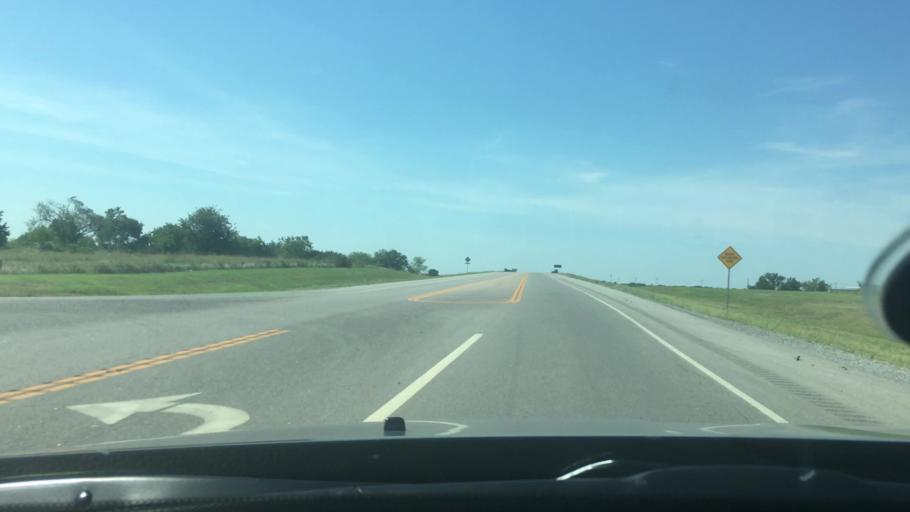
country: US
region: Oklahoma
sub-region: Bryan County
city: Durant
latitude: 33.9898
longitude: -96.3397
